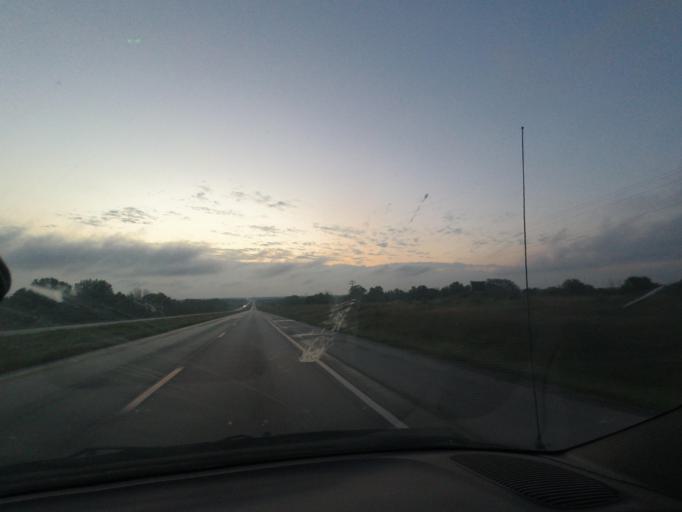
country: US
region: Missouri
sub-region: Linn County
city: Brookfield
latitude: 39.7621
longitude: -93.0061
